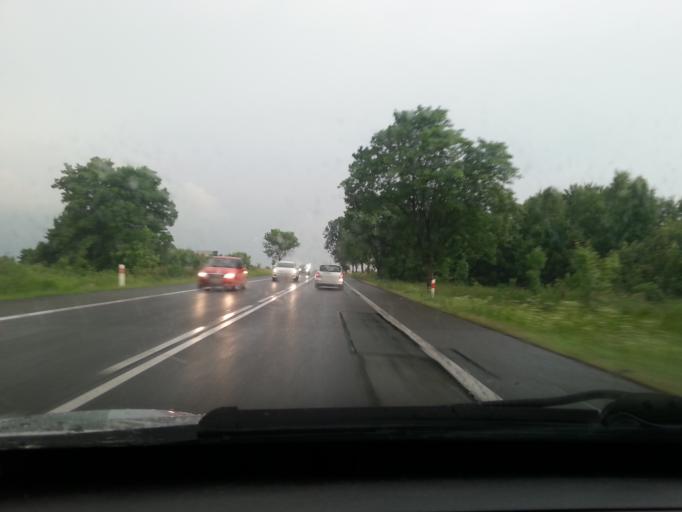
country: PL
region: Lodz Voivodeship
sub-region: Powiat zgierski
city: Strykow
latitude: 51.8520
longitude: 19.5624
